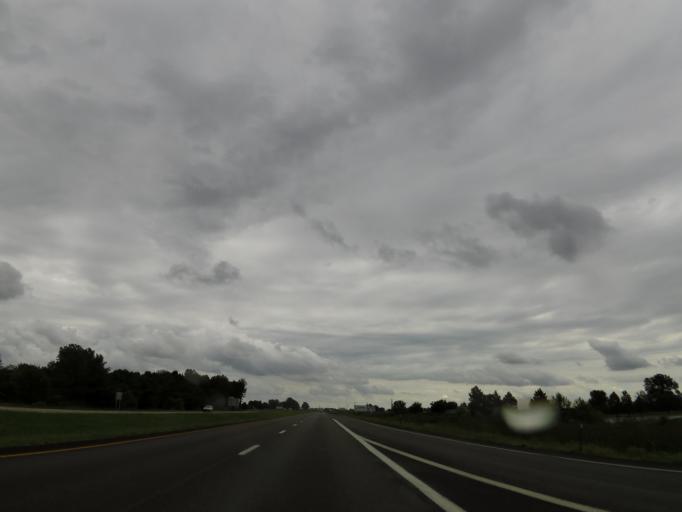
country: US
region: Missouri
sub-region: Mississippi County
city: Charleston
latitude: 36.9058
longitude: -89.3496
